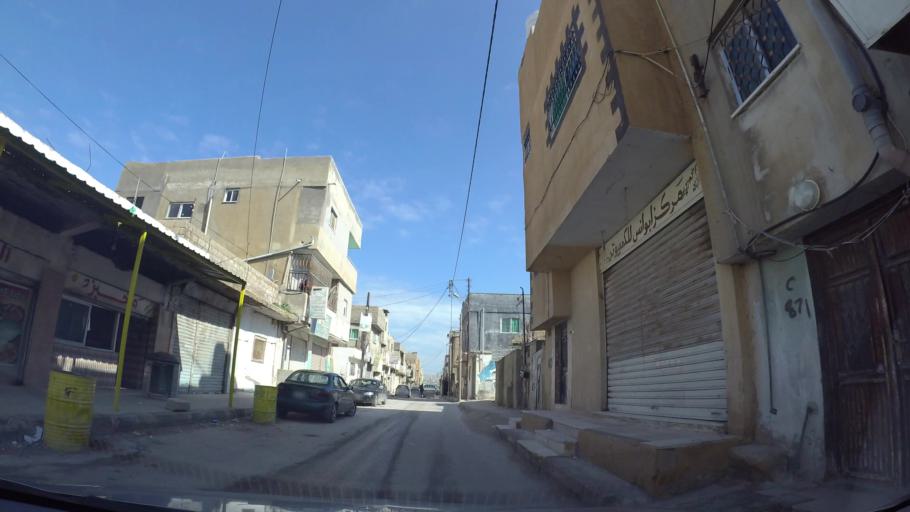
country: JO
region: Amman
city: Al Jubayhah
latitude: 32.0741
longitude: 35.8469
